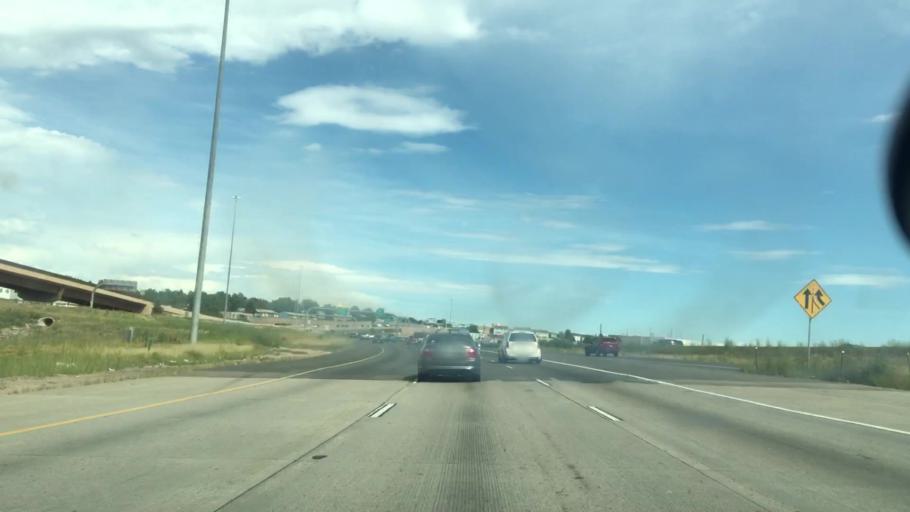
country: US
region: Colorado
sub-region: Adams County
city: Sherrelwood
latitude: 39.8286
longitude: -104.9812
